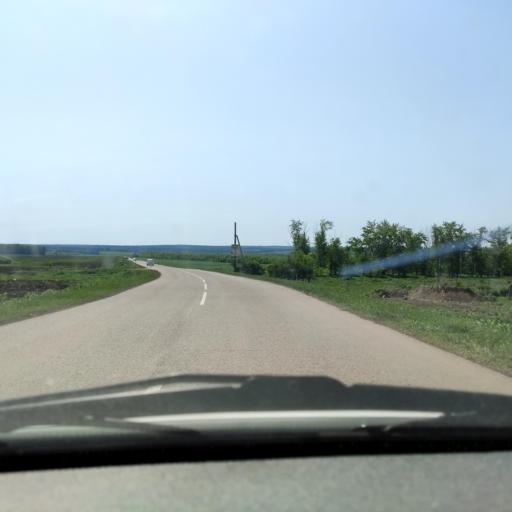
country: RU
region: Bashkortostan
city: Avdon
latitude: 54.5500
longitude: 55.6591
